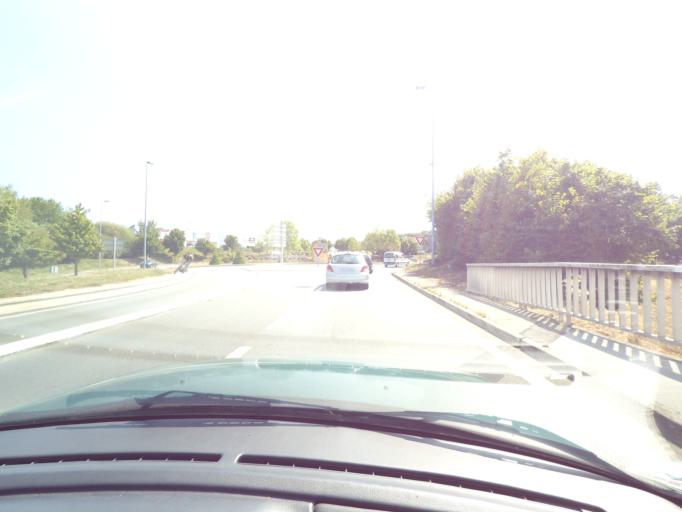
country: FR
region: Limousin
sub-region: Departement de la Haute-Vienne
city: Condat-sur-Vienne
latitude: 45.8183
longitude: 1.2935
